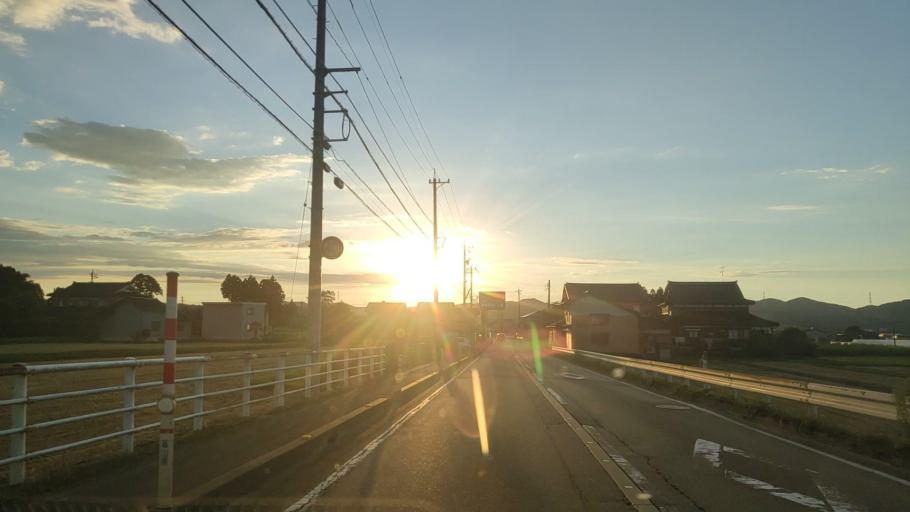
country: JP
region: Toyama
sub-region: Oyabe Shi
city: Oyabe
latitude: 36.6319
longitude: 136.8615
